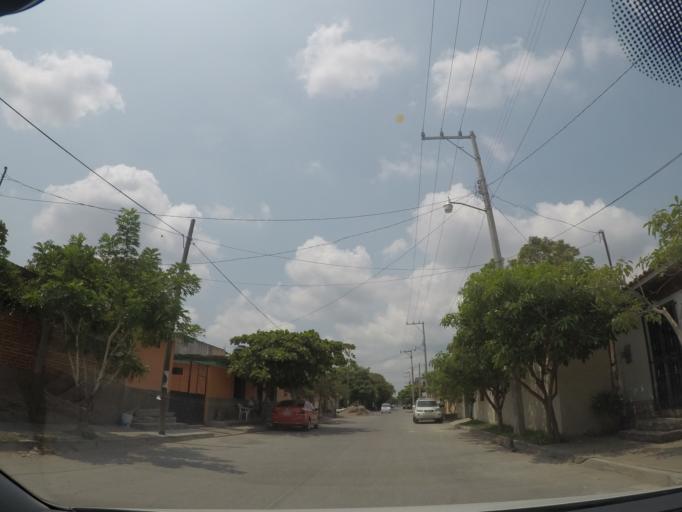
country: MX
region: Oaxaca
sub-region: El Espinal
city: El Espinal
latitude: 16.4818
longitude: -95.0438
